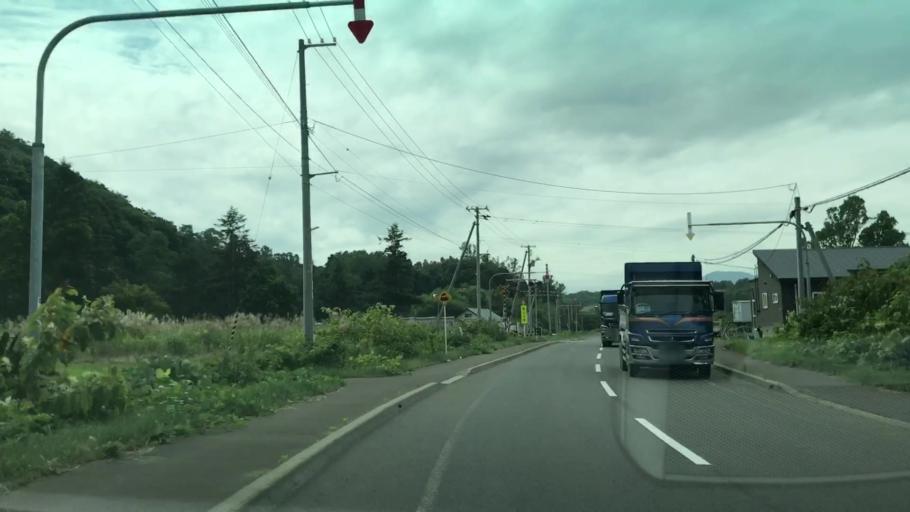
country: JP
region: Hokkaido
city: Yoichi
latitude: 43.1959
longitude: 140.8443
